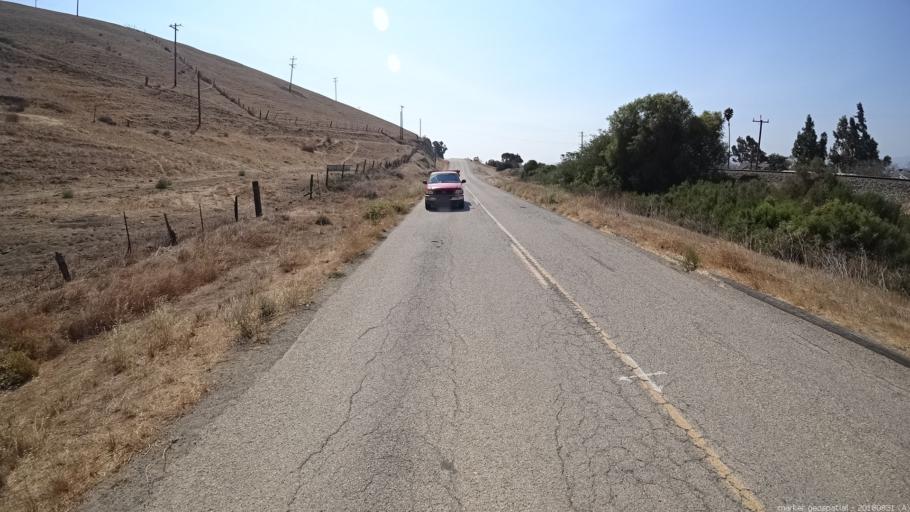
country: US
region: California
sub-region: Monterey County
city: Greenfield
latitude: 36.3650
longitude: -121.2337
